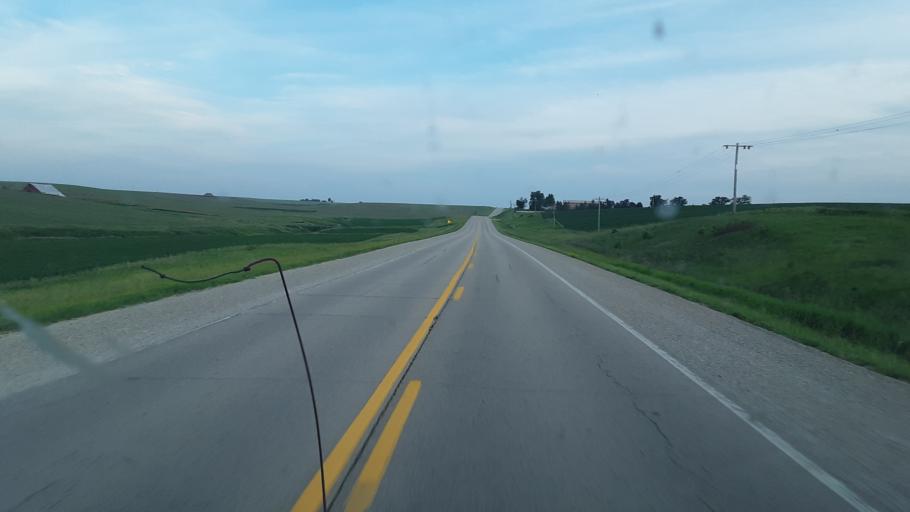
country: US
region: Iowa
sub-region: Benton County
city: Belle Plaine
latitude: 41.7759
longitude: -92.2793
